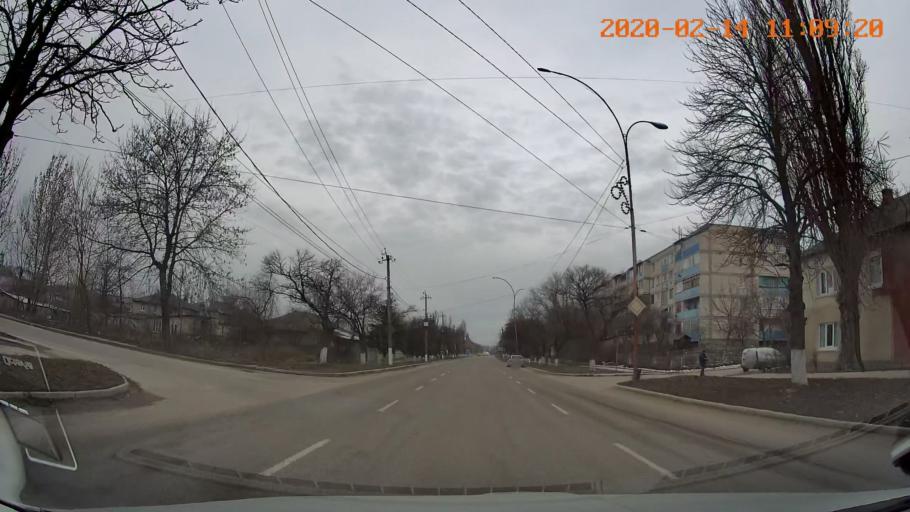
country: MD
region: Raionul Edinet
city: Edinet
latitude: 48.1775
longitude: 27.2948
